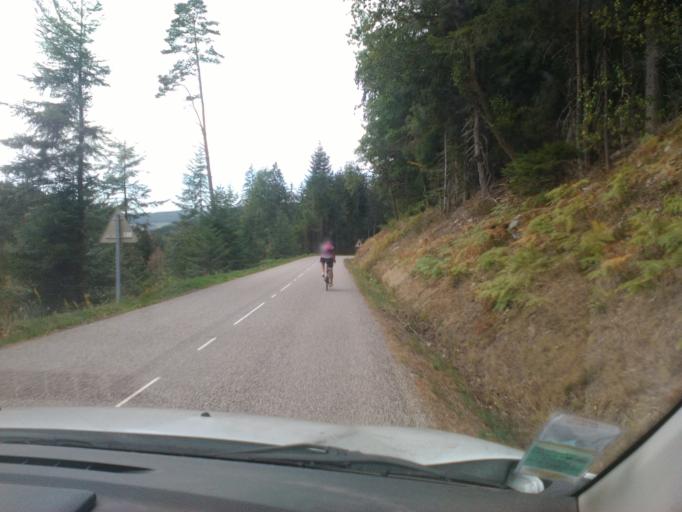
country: FR
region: Lorraine
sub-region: Departement des Vosges
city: Le Tholy
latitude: 48.1061
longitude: 6.7571
